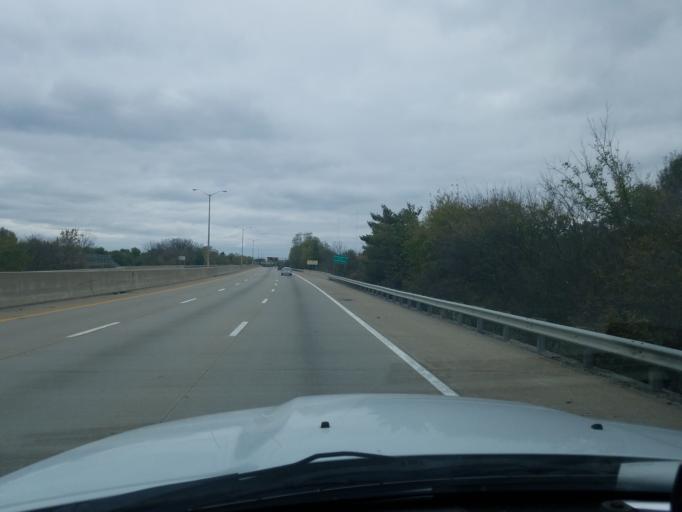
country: US
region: Kentucky
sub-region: Jefferson County
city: Shively
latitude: 38.2411
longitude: -85.8159
